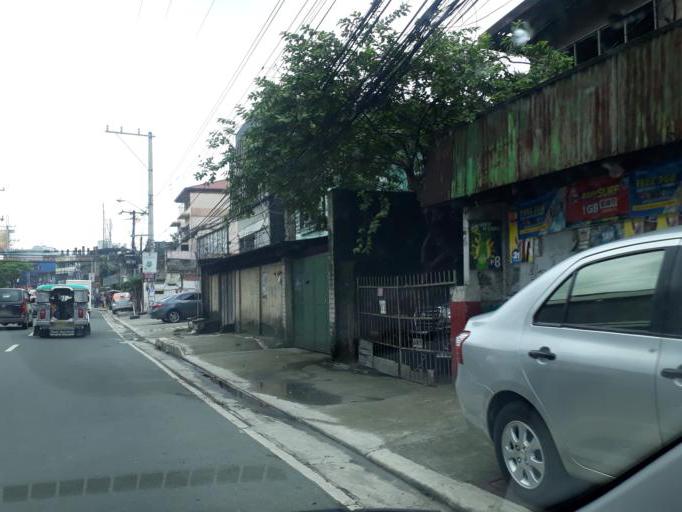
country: PH
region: Calabarzon
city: Del Monte
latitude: 14.6361
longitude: 121.0181
